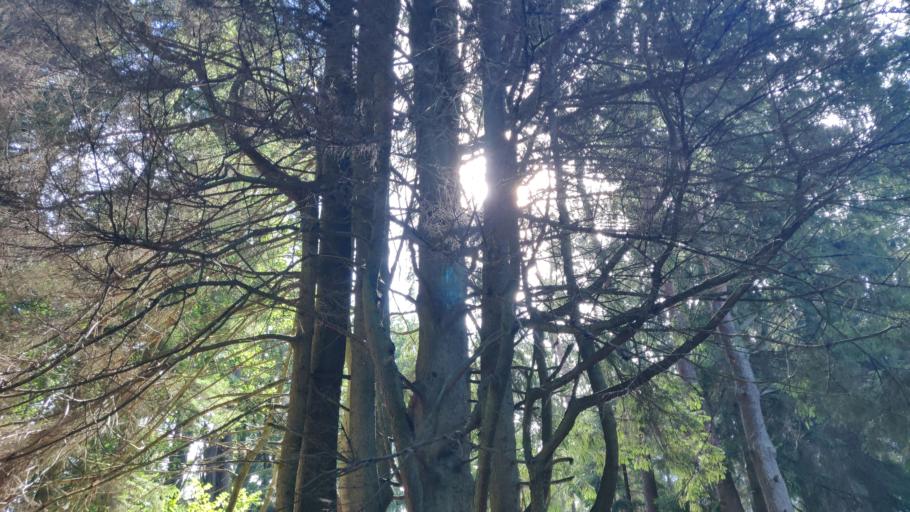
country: RU
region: Kaliningrad
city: Neman
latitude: 55.1034
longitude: 22.1471
